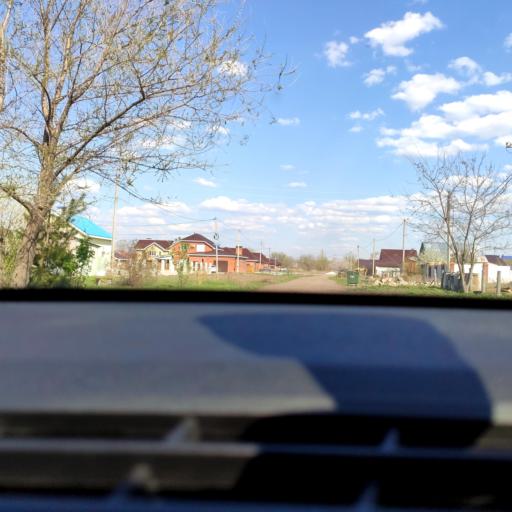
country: RU
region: Samara
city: Tol'yatti
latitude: 53.5550
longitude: 49.3785
